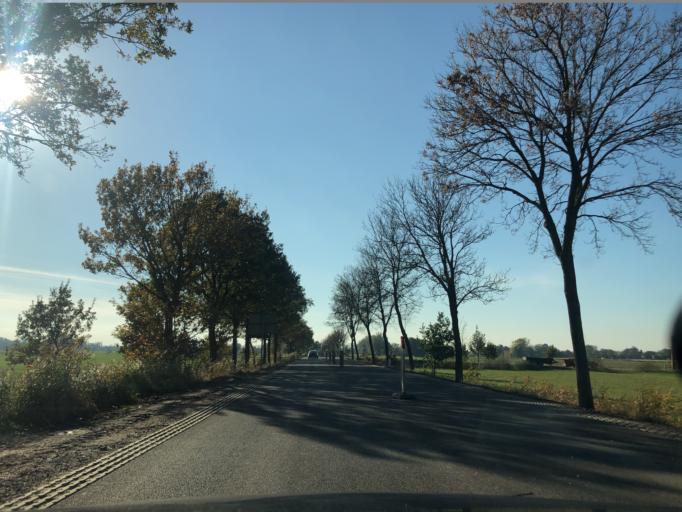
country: DE
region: Lower Saxony
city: Lemwerder
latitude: 53.1567
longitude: 8.5569
